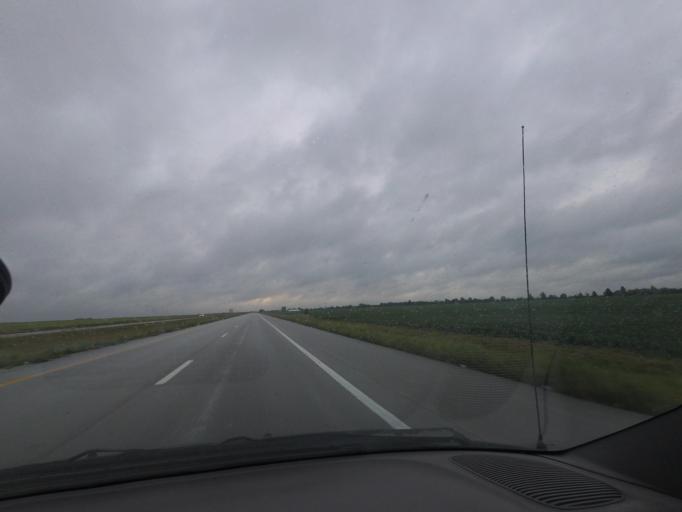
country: US
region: Missouri
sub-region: Marion County
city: Monroe City
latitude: 39.6641
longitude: -91.6940
